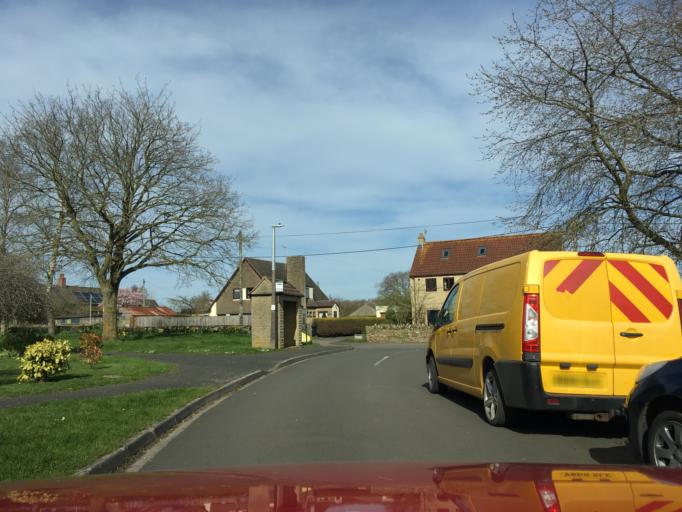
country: GB
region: England
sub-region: Wiltshire
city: Chippenham
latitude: 51.4980
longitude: -2.1443
